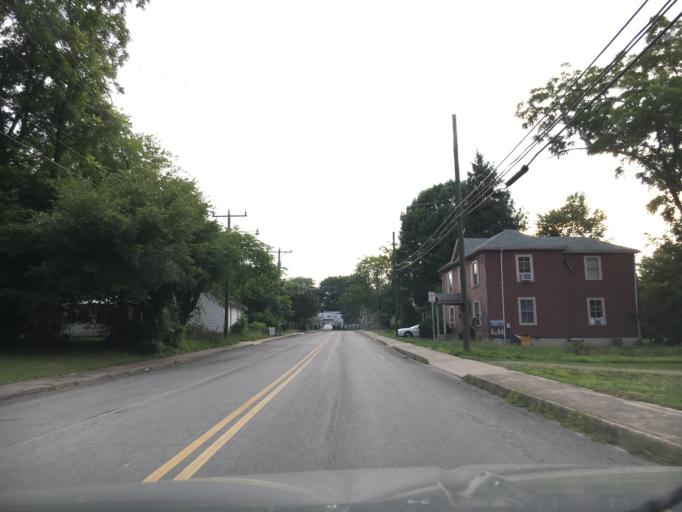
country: US
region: Virginia
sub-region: Halifax County
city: South Boston
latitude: 36.7048
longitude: -78.8969
